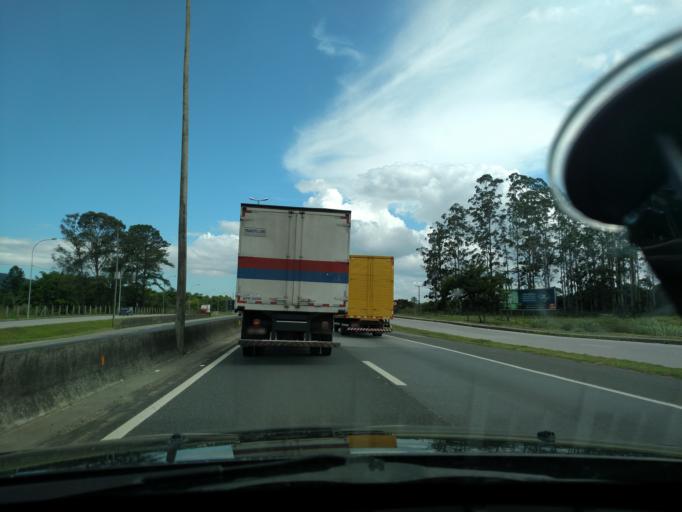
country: BR
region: Santa Catarina
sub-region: Porto Belo
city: Porto Belo
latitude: -27.1650
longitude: -48.6113
